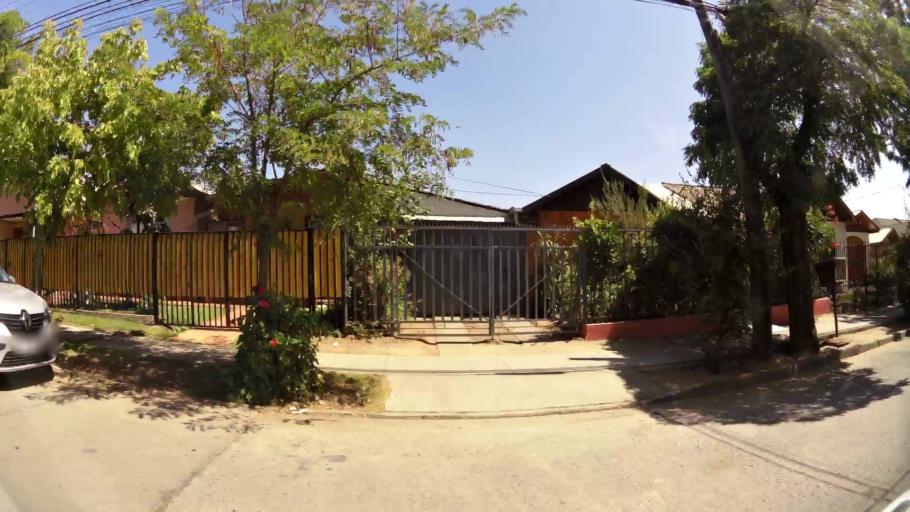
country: CL
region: Maule
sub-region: Provincia de Talca
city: Talca
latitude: -35.4303
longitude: -71.6297
